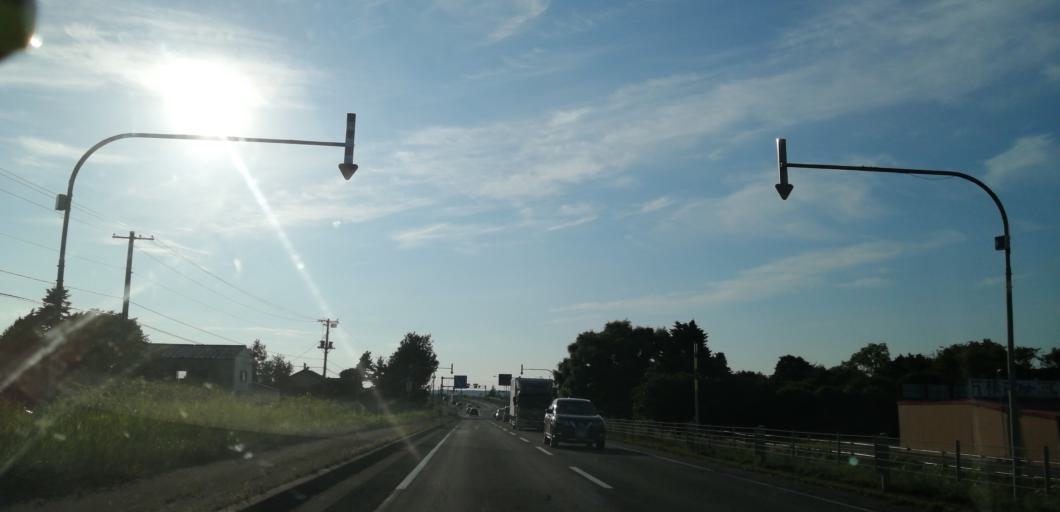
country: JP
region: Hokkaido
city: Kitahiroshima
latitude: 42.9961
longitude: 141.5918
